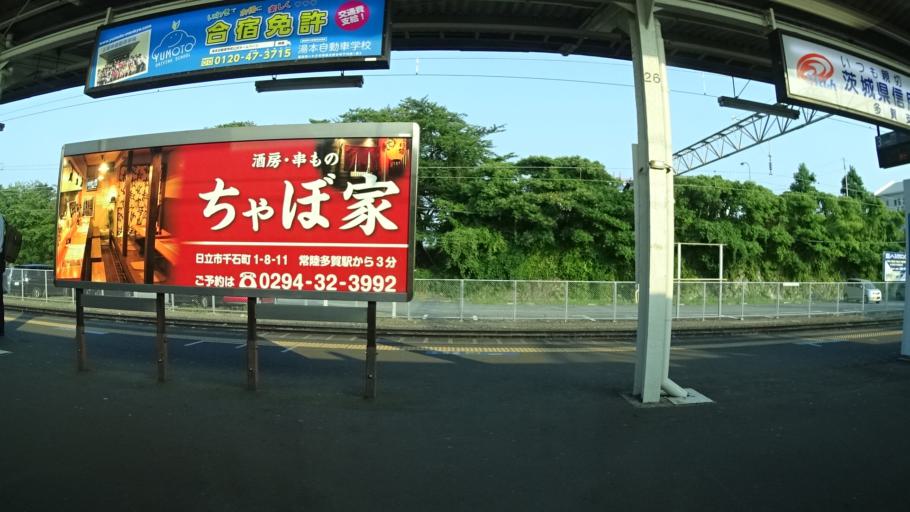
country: JP
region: Ibaraki
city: Hitachi
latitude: 36.5517
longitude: 140.6323
